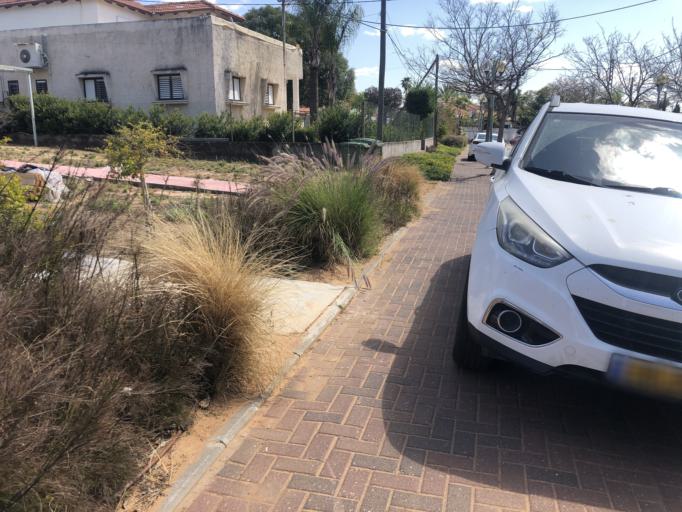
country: IL
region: Central District
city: Kfar Saba
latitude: 32.1595
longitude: 34.9206
